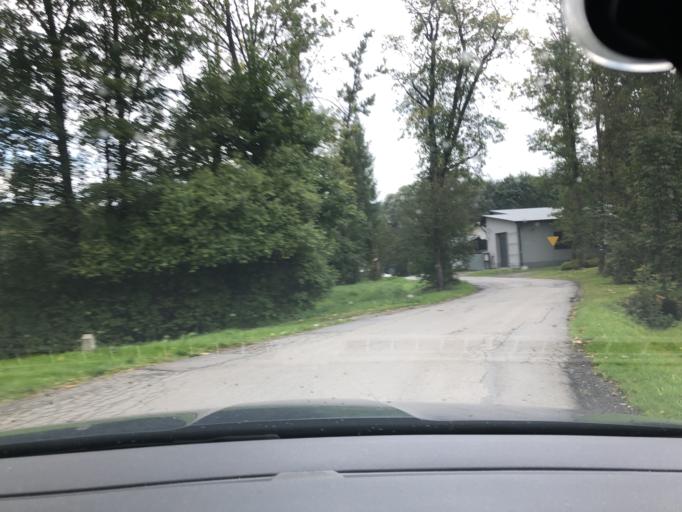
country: PL
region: Silesian Voivodeship
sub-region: Powiat zywiecki
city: Slemien
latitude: 49.7223
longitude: 19.3781
